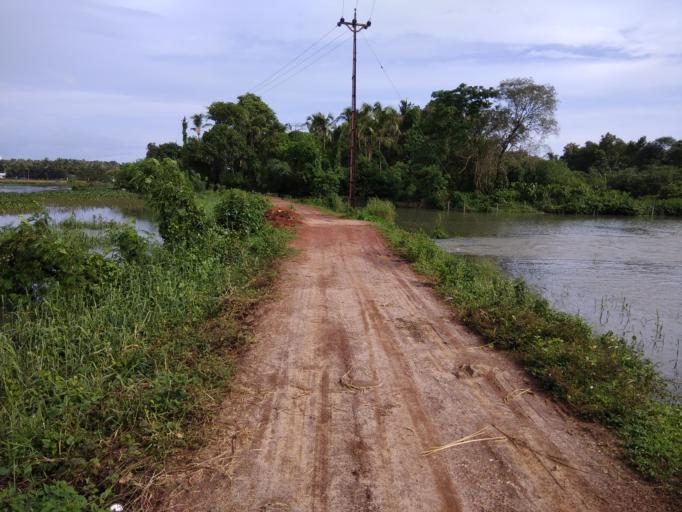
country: IN
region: Kerala
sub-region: Thrissur District
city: Trichur
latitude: 10.5354
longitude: 76.1776
